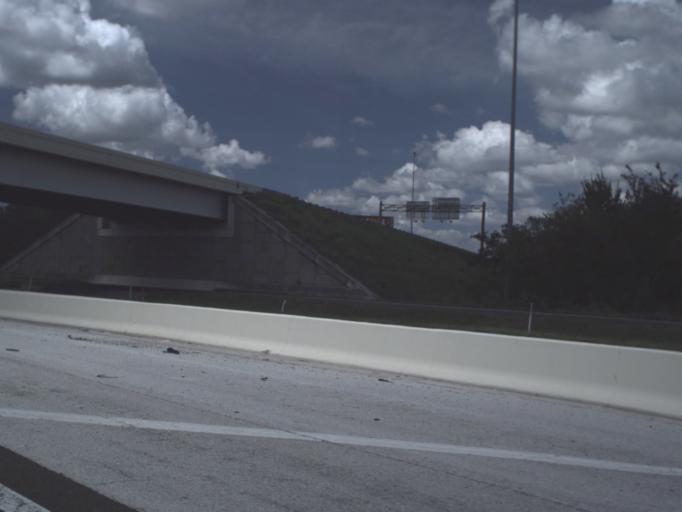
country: US
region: Florida
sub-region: Hillsborough County
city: East Lake-Orient Park
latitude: 27.9954
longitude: -82.3662
